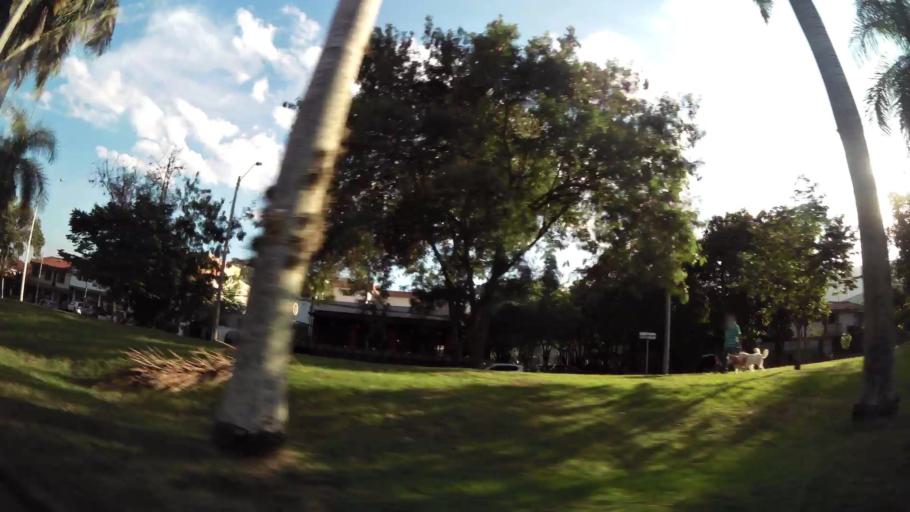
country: CO
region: Valle del Cauca
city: Cali
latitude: 3.4884
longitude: -76.5219
